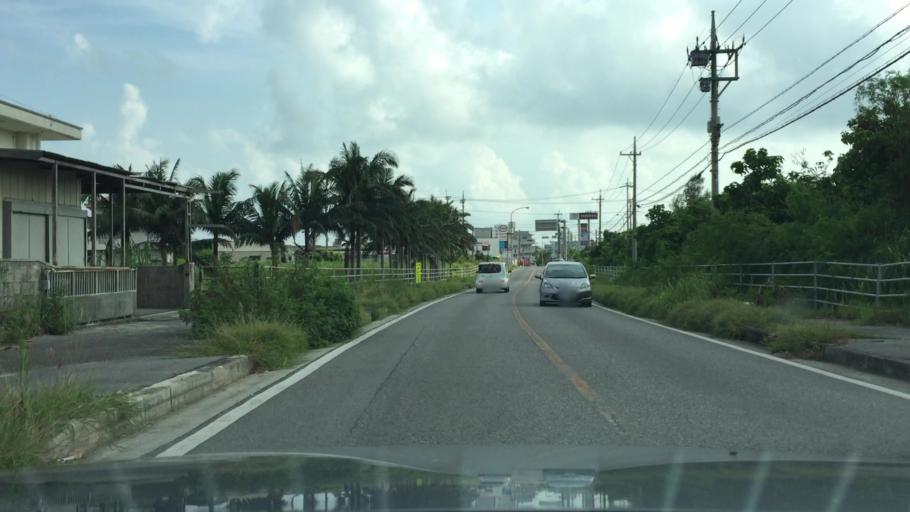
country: JP
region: Okinawa
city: Ishigaki
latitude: 24.3488
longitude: 124.1698
